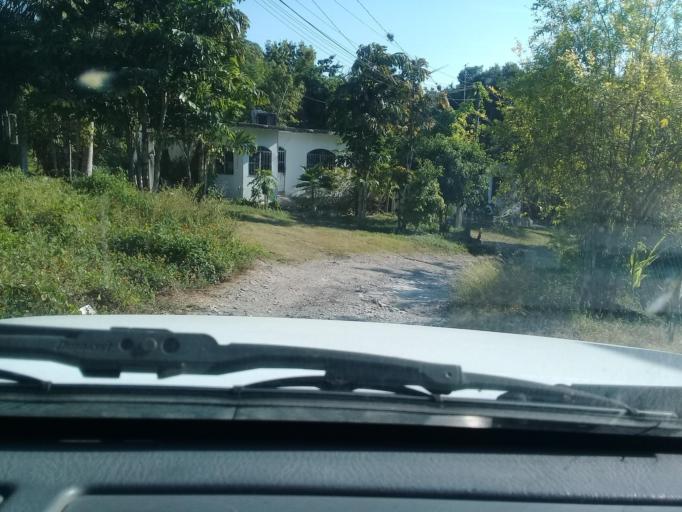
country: MX
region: Veracruz
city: Rinconada
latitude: 19.4015
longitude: -96.5569
